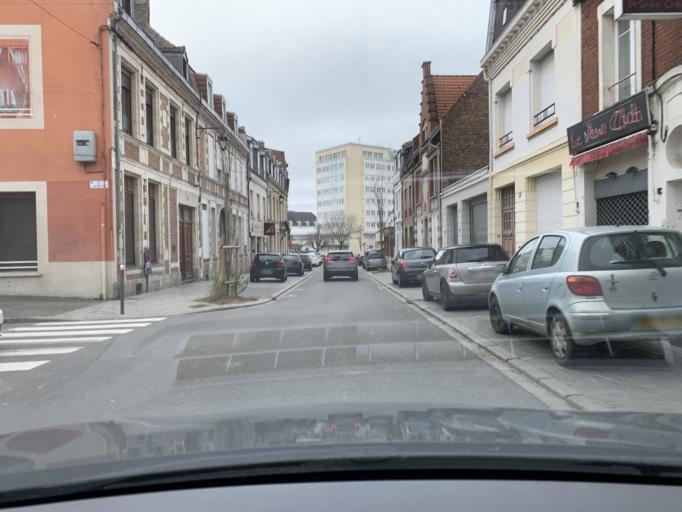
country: FR
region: Nord-Pas-de-Calais
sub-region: Departement du Nord
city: Cambrai
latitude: 50.1748
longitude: 3.2315
